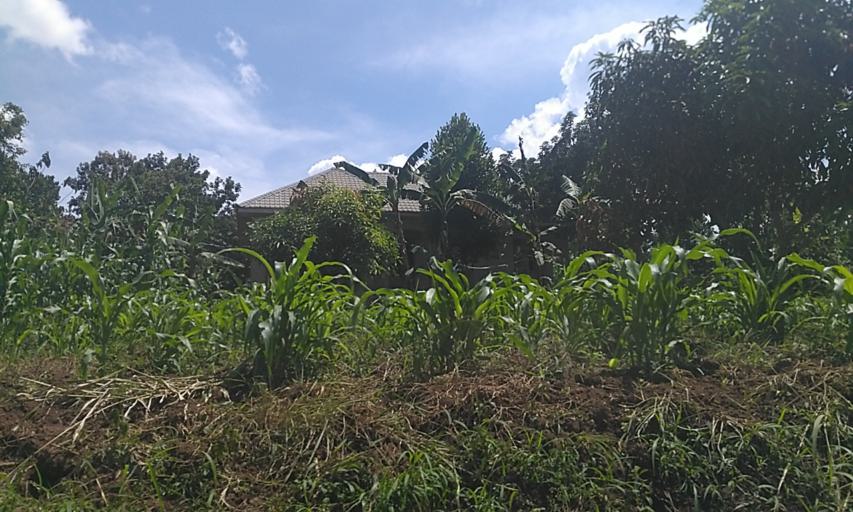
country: UG
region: Central Region
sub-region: Wakiso District
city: Wakiso
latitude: 0.4105
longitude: 32.4740
